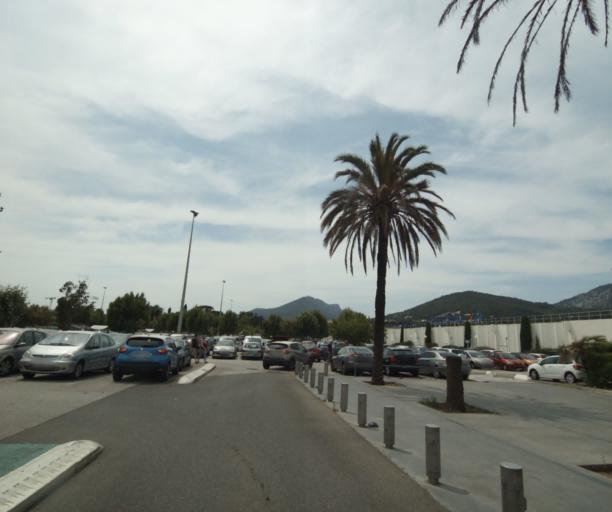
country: FR
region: Provence-Alpes-Cote d'Azur
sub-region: Departement du Var
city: La Garde
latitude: 43.1412
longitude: 6.0162
